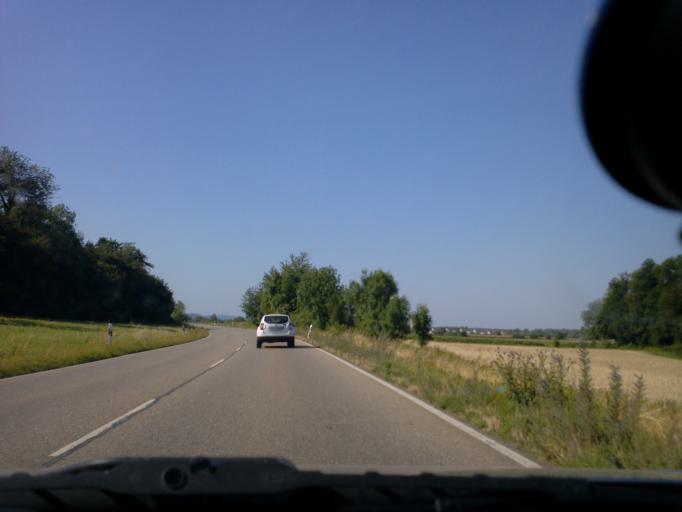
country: DE
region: Baden-Wuerttemberg
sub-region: Karlsruhe Region
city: Weingarten
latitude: 49.0689
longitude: 8.5402
